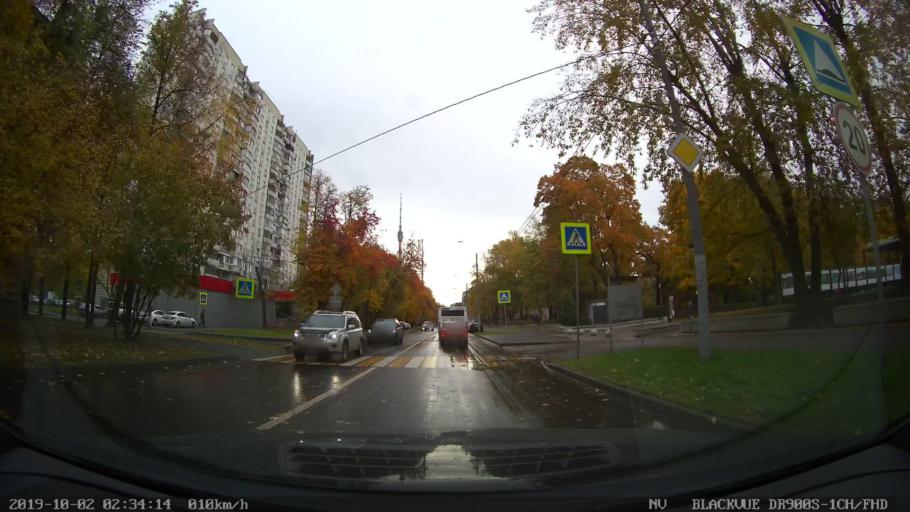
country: RU
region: Moscow
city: Ostankinskiy
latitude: 55.8152
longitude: 37.5864
